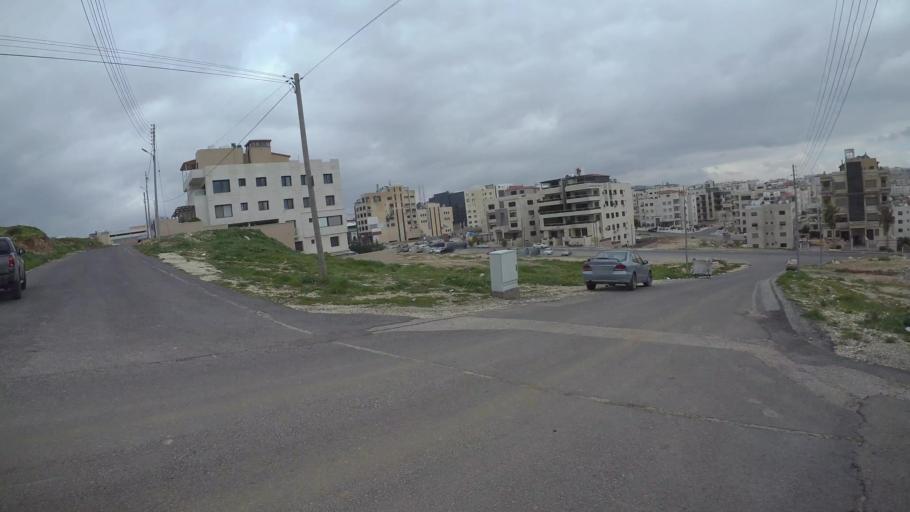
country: JO
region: Amman
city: Al Jubayhah
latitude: 31.9940
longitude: 35.8357
